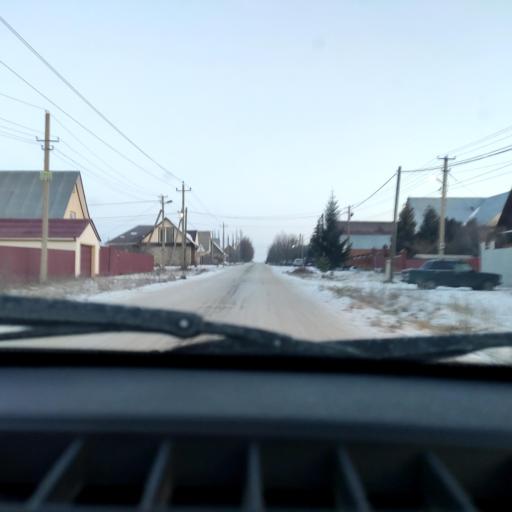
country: RU
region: Bashkortostan
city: Avdon
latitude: 54.6594
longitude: 55.7706
